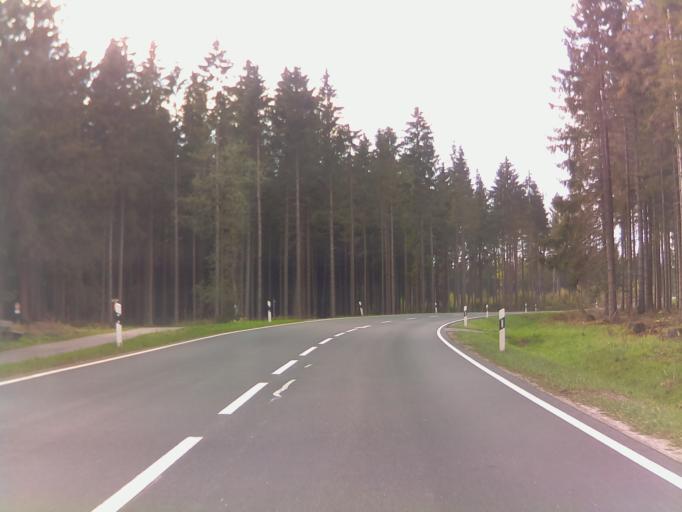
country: DE
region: Bavaria
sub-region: Upper Franconia
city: Ludwigsstadt
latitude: 50.4442
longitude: 11.3653
